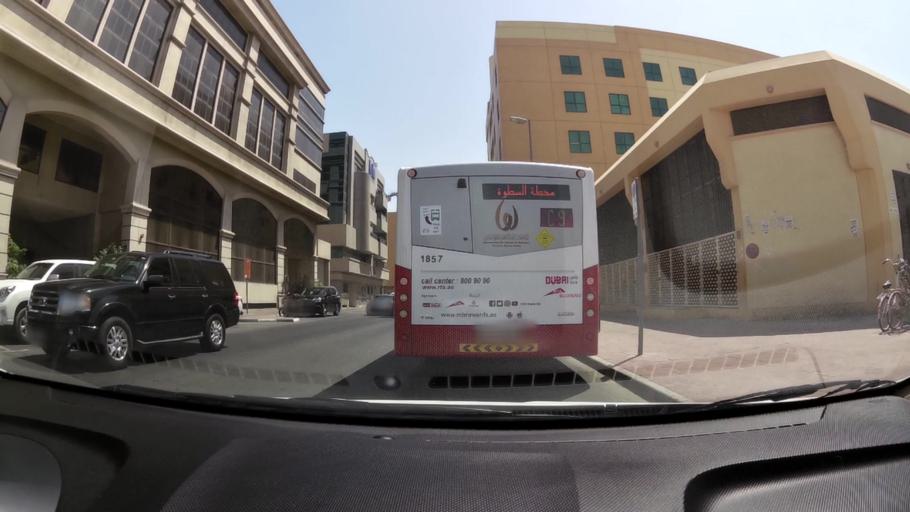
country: AE
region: Ash Shariqah
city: Sharjah
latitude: 25.2787
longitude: 55.3515
